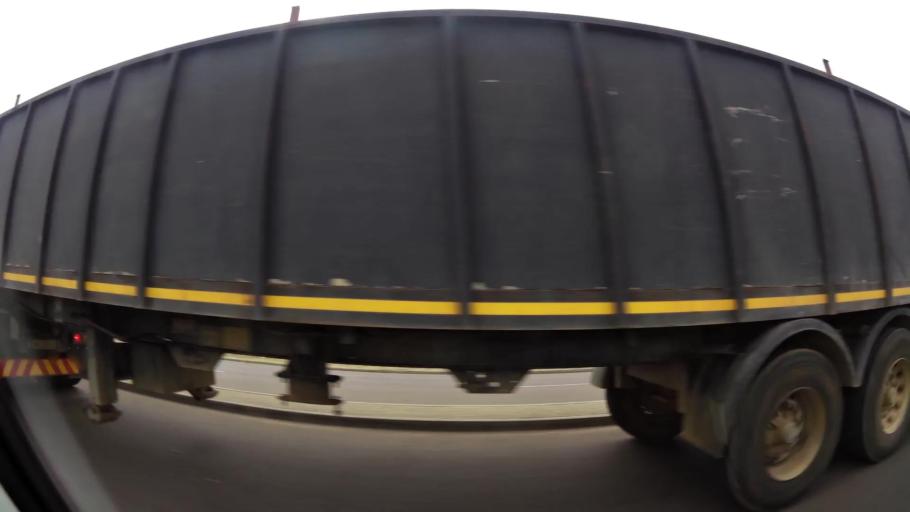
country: ZA
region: Limpopo
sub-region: Capricorn District Municipality
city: Polokwane
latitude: -23.8864
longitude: 29.4305
